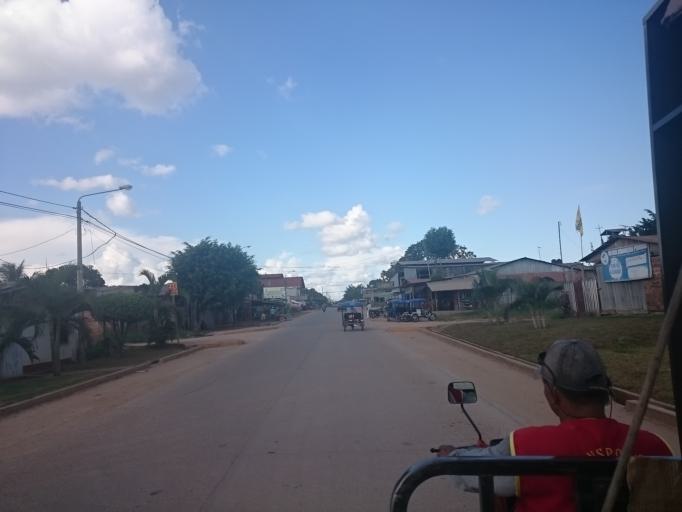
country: PE
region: Ucayali
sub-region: Provincia de Coronel Portillo
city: Pucallpa
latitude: -8.3821
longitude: -74.5650
